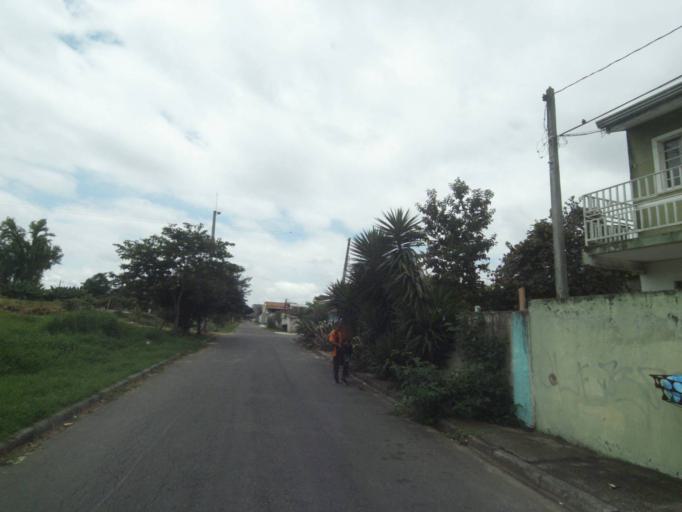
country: BR
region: Parana
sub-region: Pinhais
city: Pinhais
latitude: -25.4516
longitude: -49.2012
